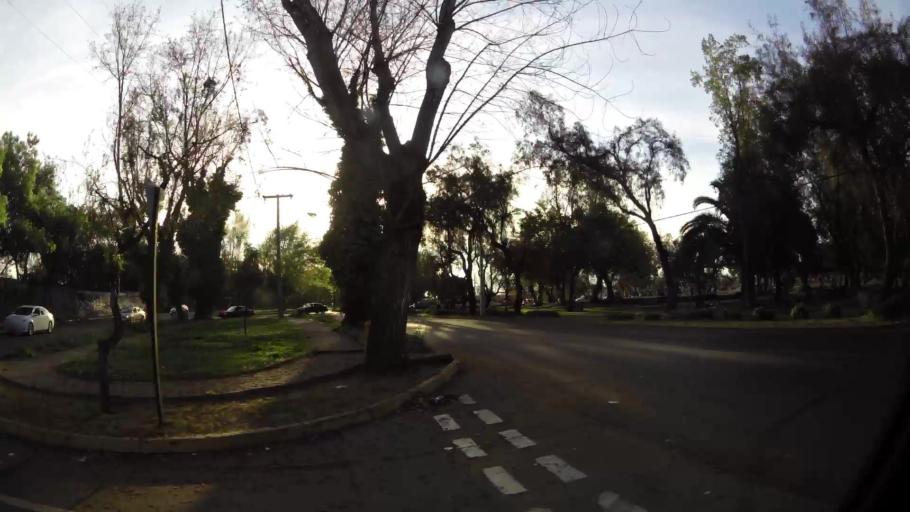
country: CL
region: Santiago Metropolitan
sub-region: Provincia de Santiago
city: Lo Prado
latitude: -33.4557
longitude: -70.7218
